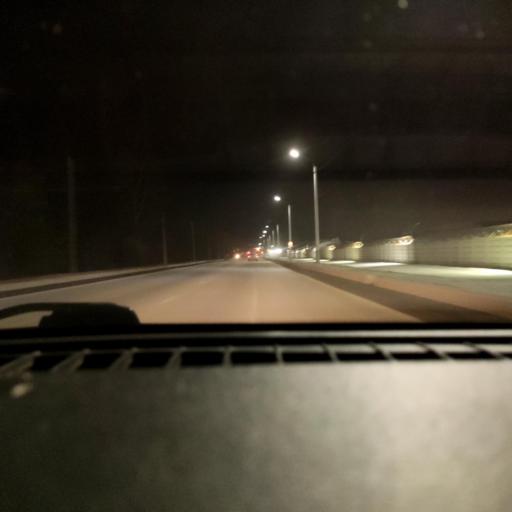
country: RU
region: Perm
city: Gamovo
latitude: 57.9188
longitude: 56.1479
